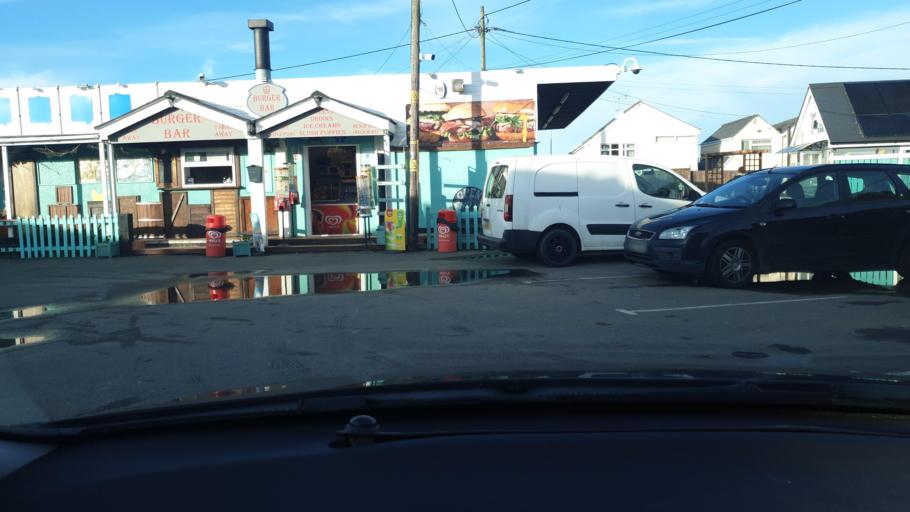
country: GB
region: England
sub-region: Essex
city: Brightlingsea
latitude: 51.8012
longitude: 1.0196
